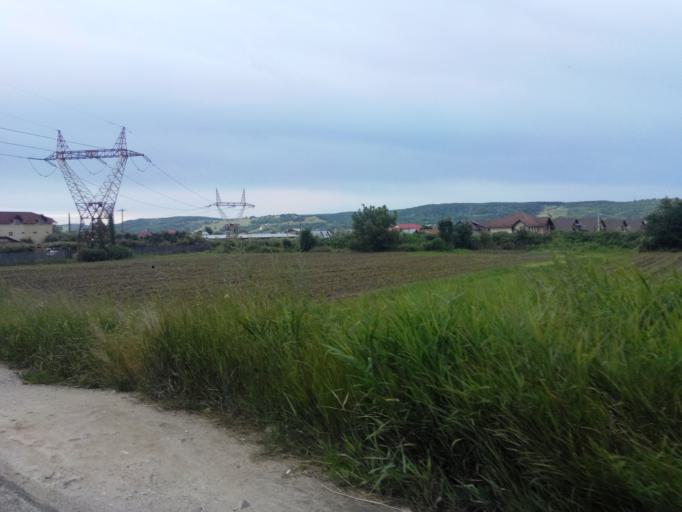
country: RO
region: Arges
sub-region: Comuna Bascov
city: Bascov
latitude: 44.9048
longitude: 24.8124
